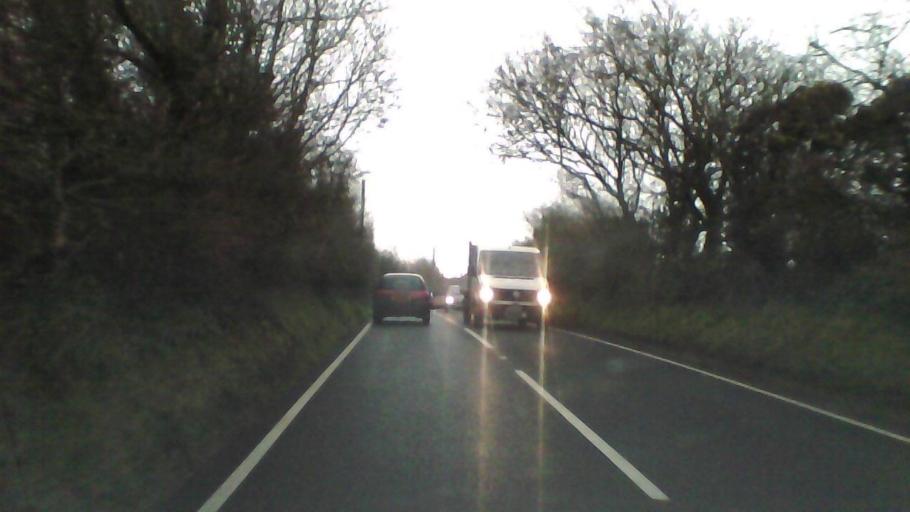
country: GB
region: England
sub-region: Isle of Wight
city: Newport
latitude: 50.6904
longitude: -1.2503
